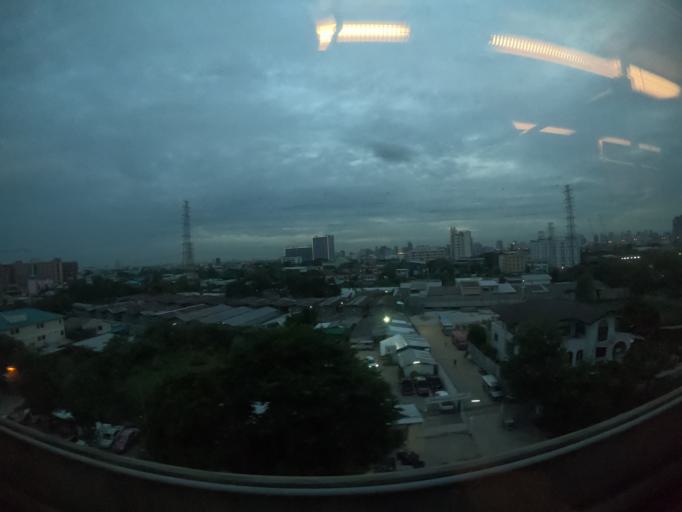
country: TH
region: Bangkok
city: Watthana
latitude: 13.7417
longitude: 100.6113
